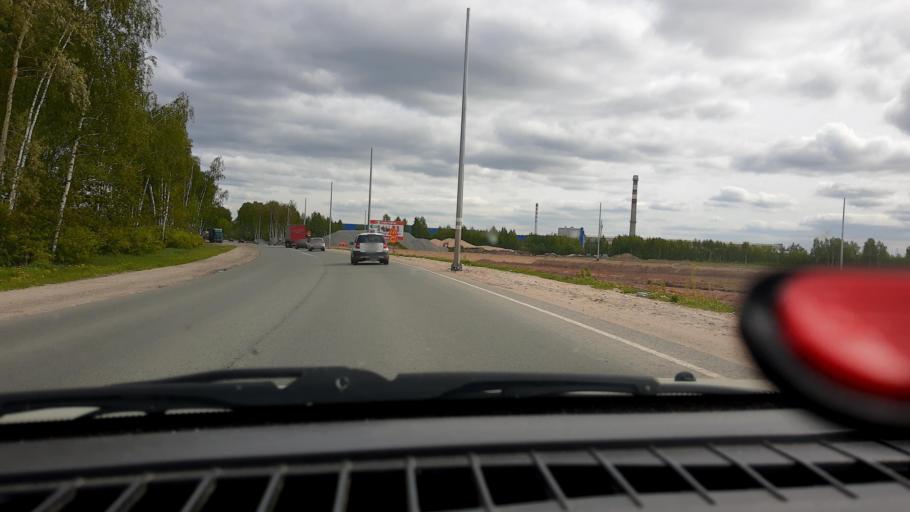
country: RU
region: Nizjnij Novgorod
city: Neklyudovo
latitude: 56.4229
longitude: 43.9936
